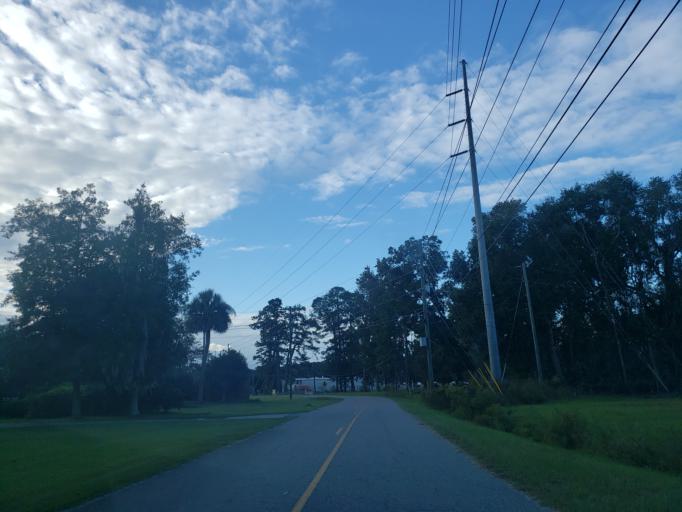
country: US
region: Georgia
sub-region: Chatham County
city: Georgetown
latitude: 31.9888
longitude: -81.2260
